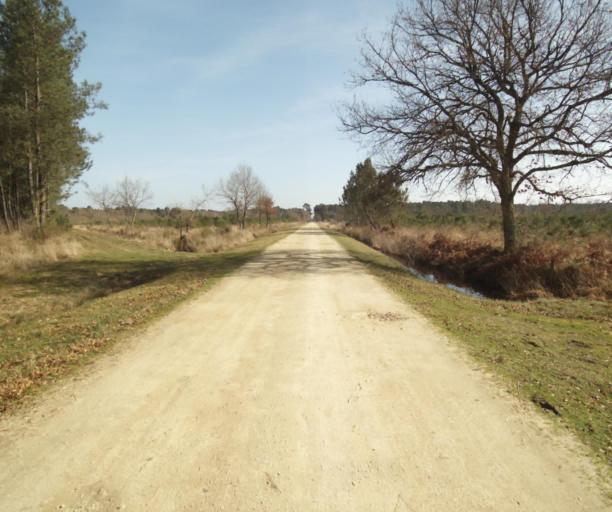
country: FR
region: Aquitaine
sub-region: Departement de la Gironde
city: Bazas
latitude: 44.2241
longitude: -0.2329
